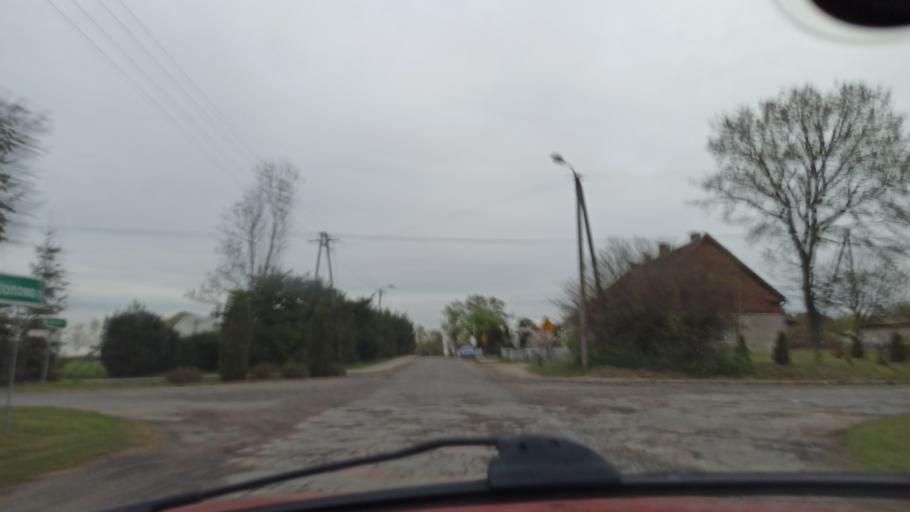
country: PL
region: Kujawsko-Pomorskie
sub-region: Powiat grudziadzki
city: Lasin
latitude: 53.5610
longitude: 19.0724
